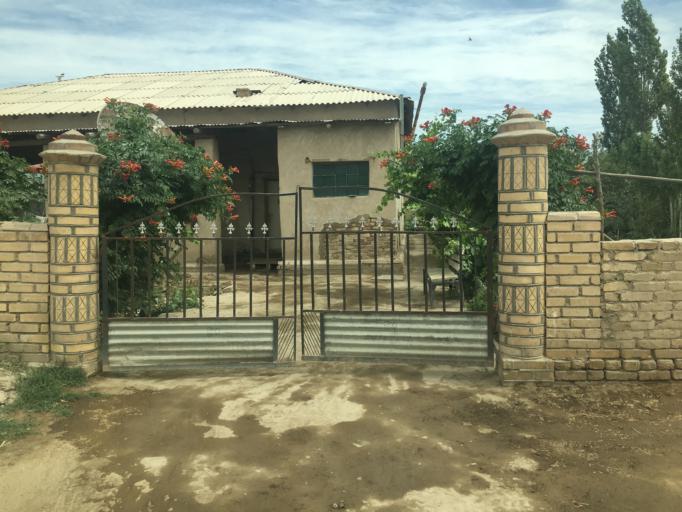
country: TM
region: Dasoguz
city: Tagta
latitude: 41.6135
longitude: 59.8283
